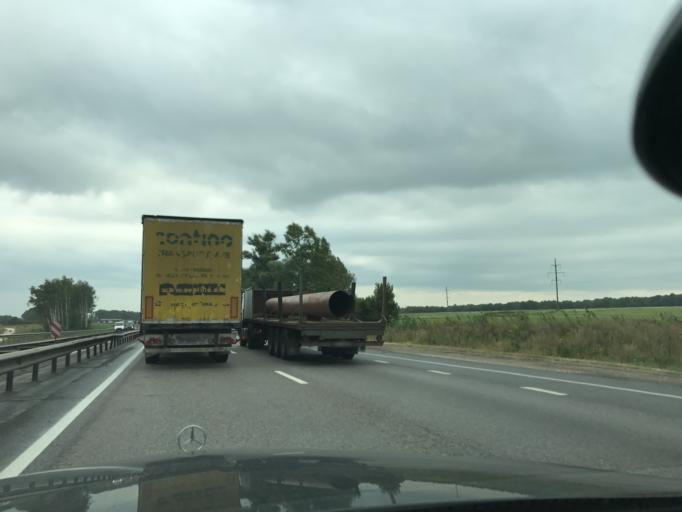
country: RU
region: Vladimir
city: Gorokhovets
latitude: 56.1717
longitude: 42.6431
